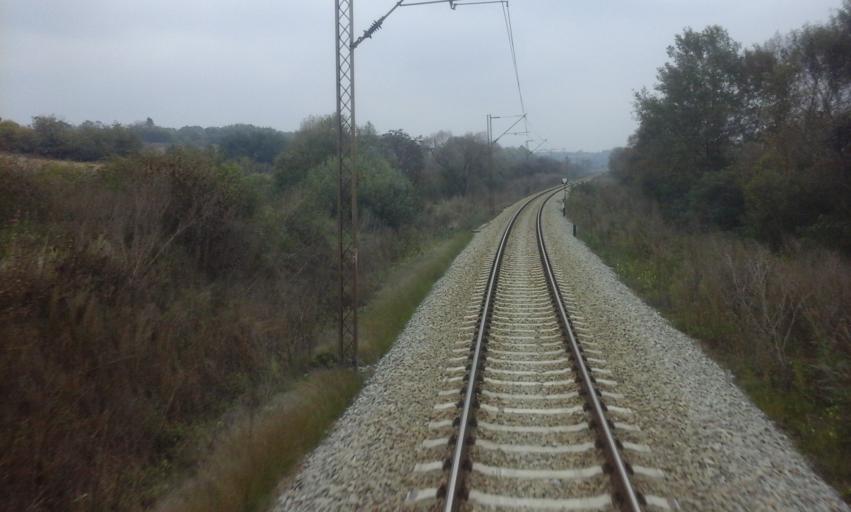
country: RS
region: Central Serbia
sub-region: Belgrade
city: Sopot
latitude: 44.4994
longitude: 20.6452
